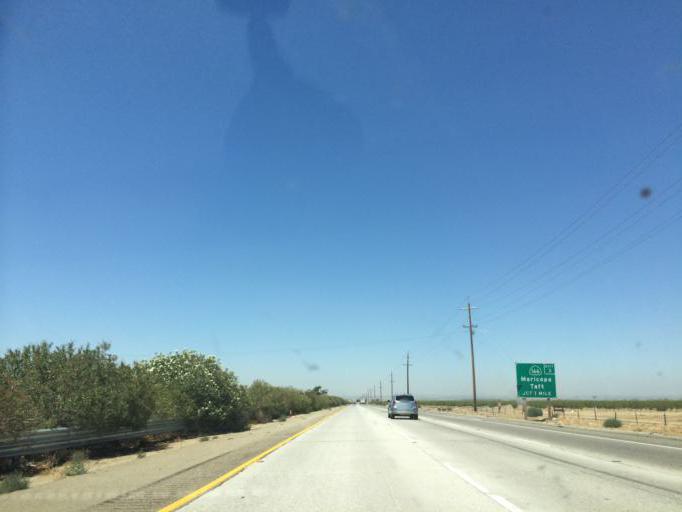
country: US
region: California
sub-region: Kern County
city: Weedpatch
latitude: 35.0332
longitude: -118.9601
